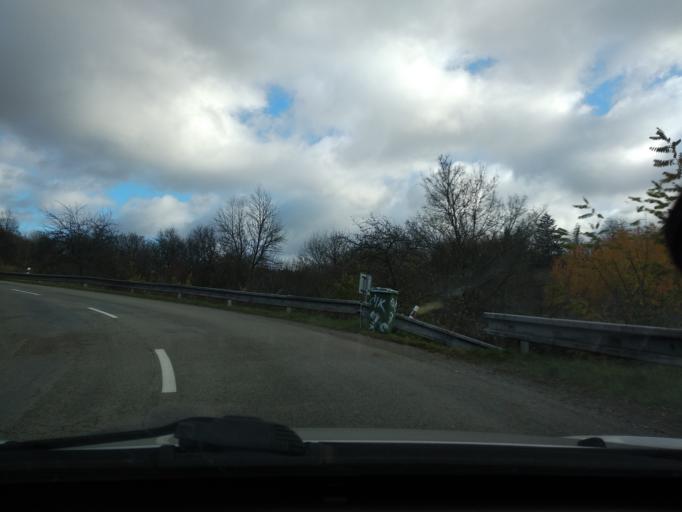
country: CZ
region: South Moravian
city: Drasov
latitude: 49.3758
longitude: 16.4694
